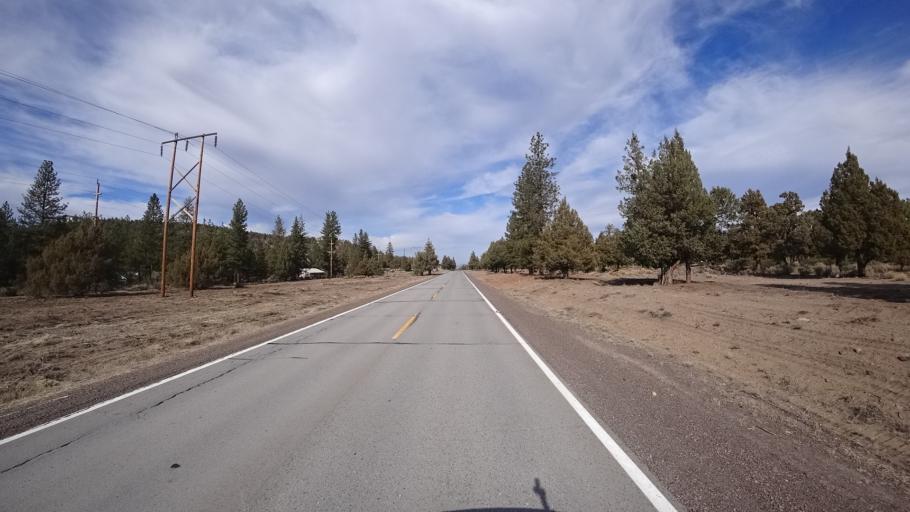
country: US
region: California
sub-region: Siskiyou County
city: Weed
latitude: 41.5330
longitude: -122.3647
